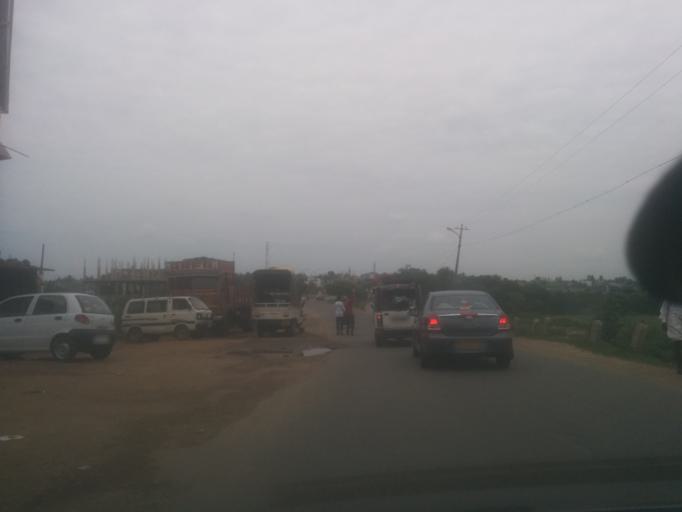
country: IN
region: Karnataka
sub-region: Hassan
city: Belur
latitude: 13.1672
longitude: 75.8703
